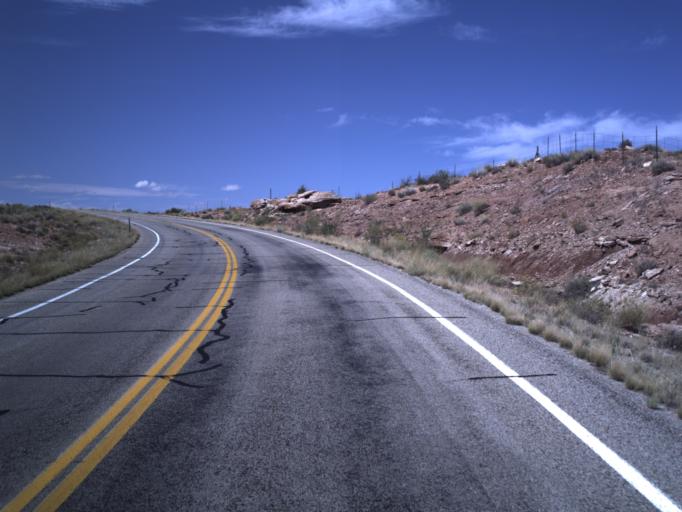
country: US
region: Utah
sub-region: San Juan County
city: Blanding
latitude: 37.2914
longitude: -109.4094
